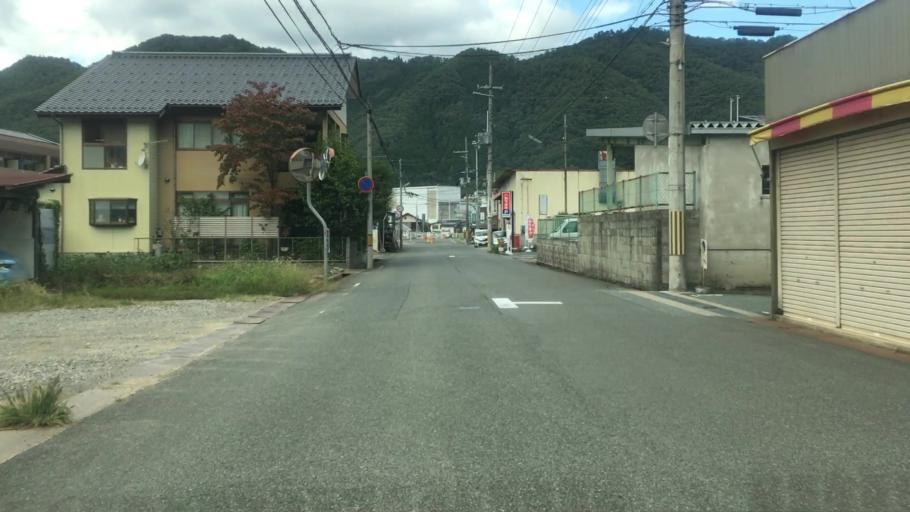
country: JP
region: Hyogo
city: Toyooka
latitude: 35.4006
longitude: 134.7678
